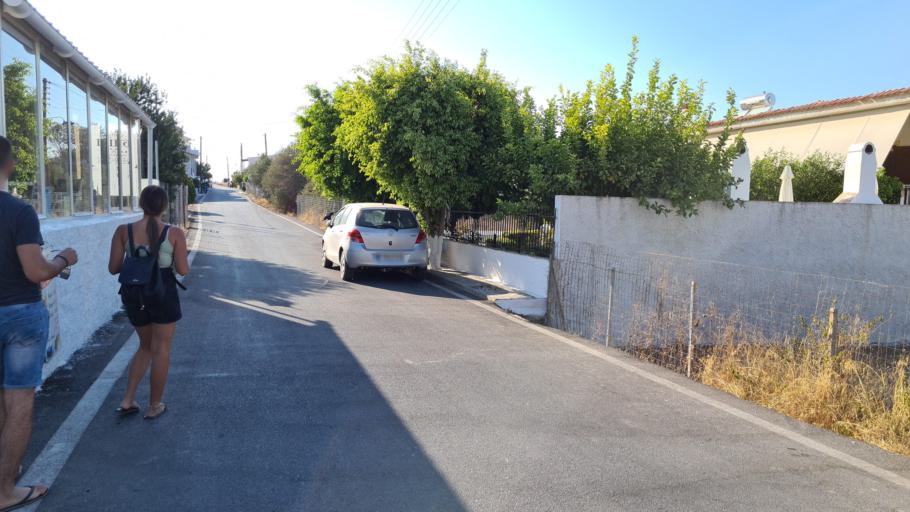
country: GR
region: Attica
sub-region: Nomos Piraios
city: Megalochori
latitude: 37.7086
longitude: 23.3611
